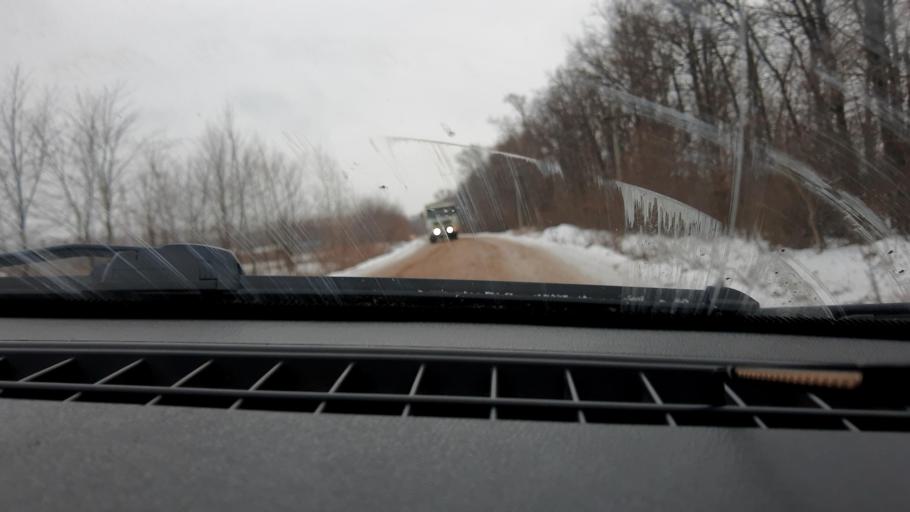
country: RU
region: Bashkortostan
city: Iglino
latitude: 54.7326
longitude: 56.2544
